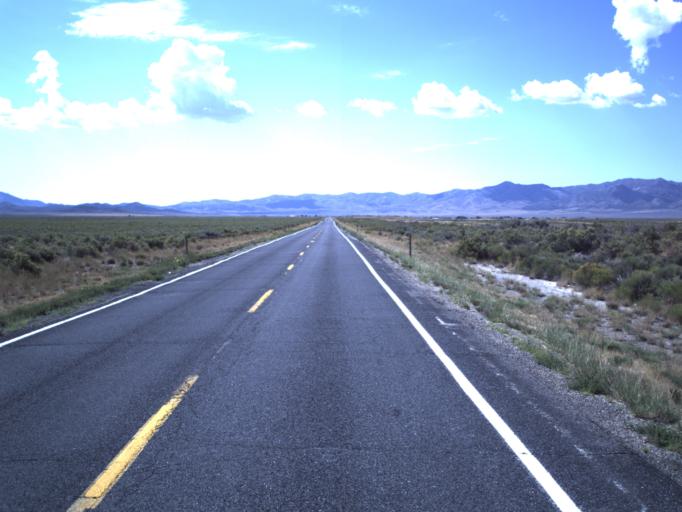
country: US
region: Utah
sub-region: Tooele County
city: Tooele
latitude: 40.1534
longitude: -112.4308
